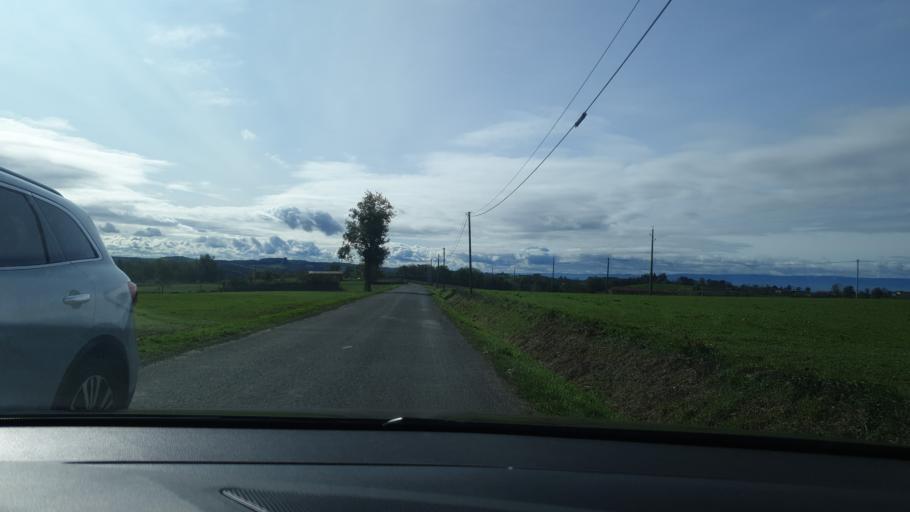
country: FR
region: Rhone-Alpes
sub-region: Departement du Rhone
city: Haute-Rivoire
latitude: 45.7277
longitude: 4.3780
